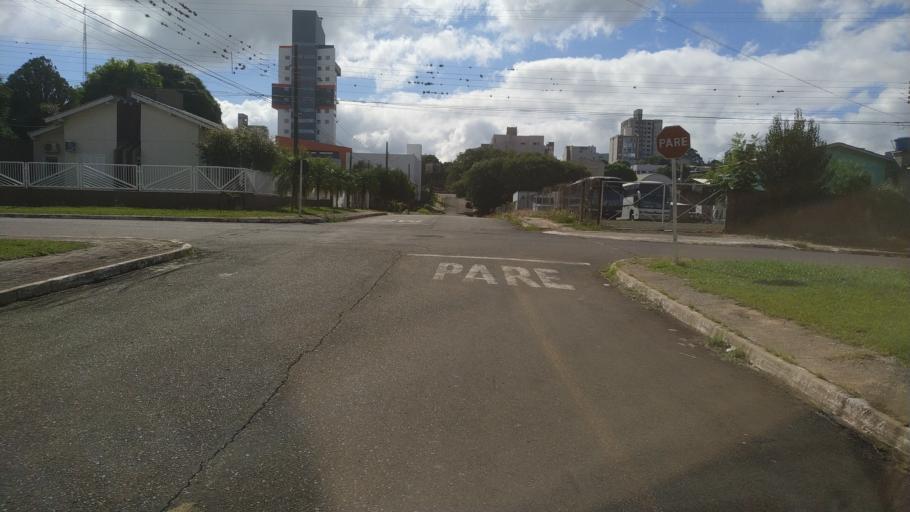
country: BR
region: Santa Catarina
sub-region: Chapeco
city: Chapeco
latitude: -27.0964
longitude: -52.6351
